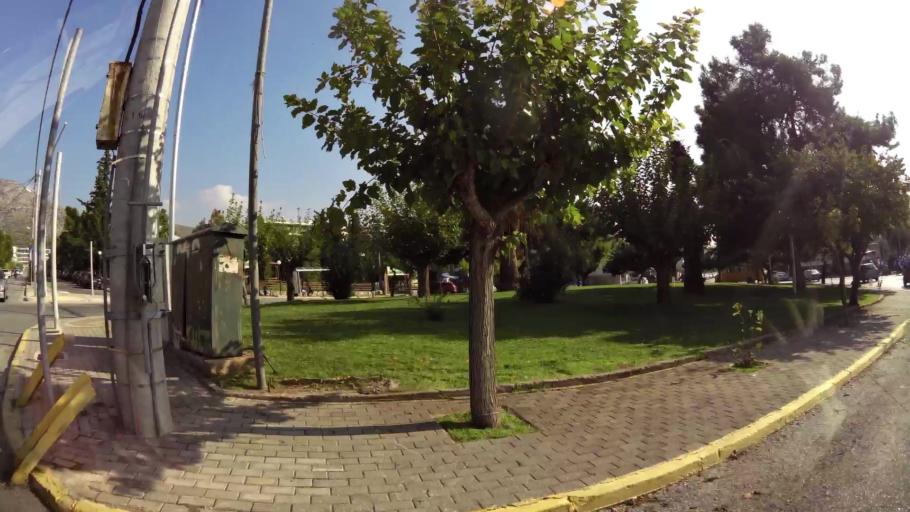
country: GR
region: Attica
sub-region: Nomarchia Athinas
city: Argyroupoli
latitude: 37.9151
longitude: 23.7500
